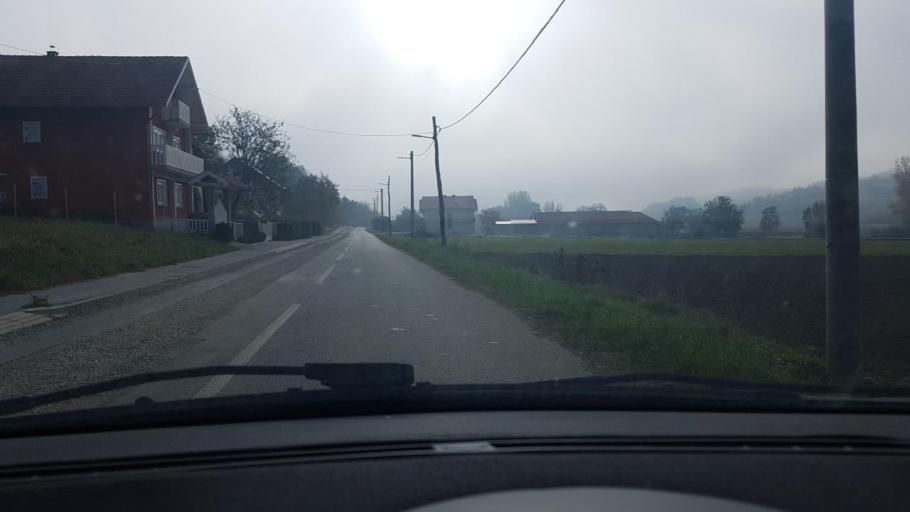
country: HR
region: Krapinsko-Zagorska
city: Zlatar
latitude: 46.1405
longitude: 16.0679
